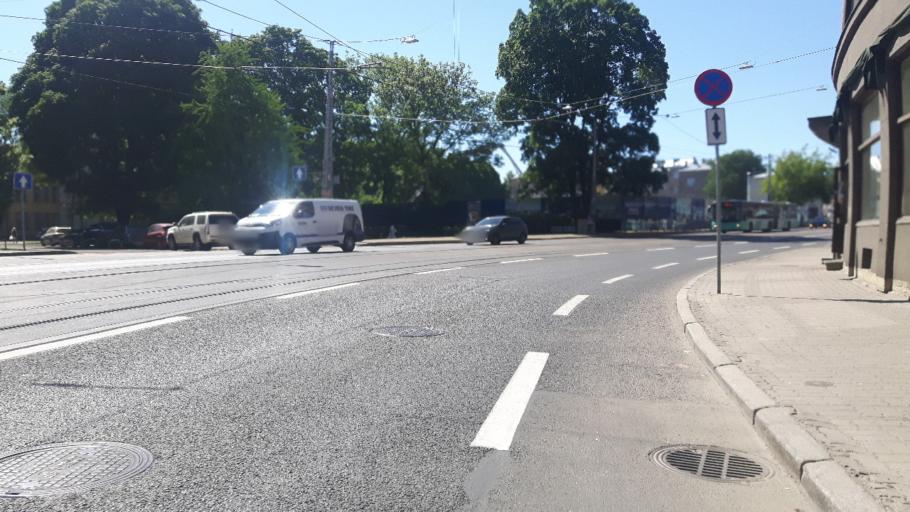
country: EE
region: Harju
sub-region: Tallinna linn
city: Tallinn
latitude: 59.4307
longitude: 24.7451
